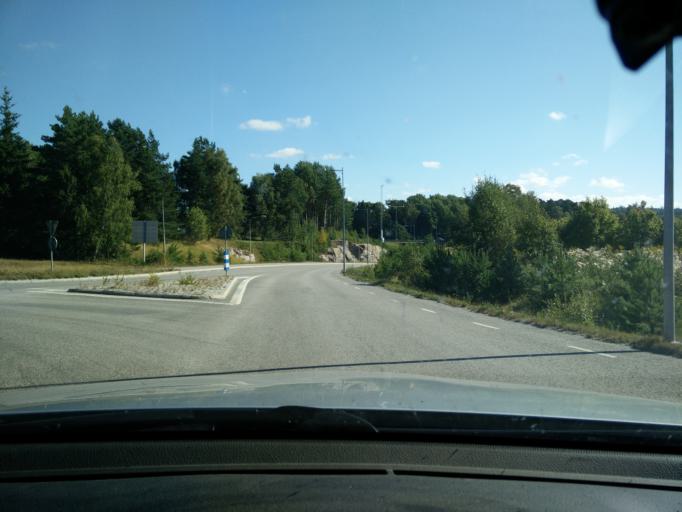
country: SE
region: Stockholm
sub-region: Taby Kommun
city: Taby
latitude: 59.4652
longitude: 18.1465
